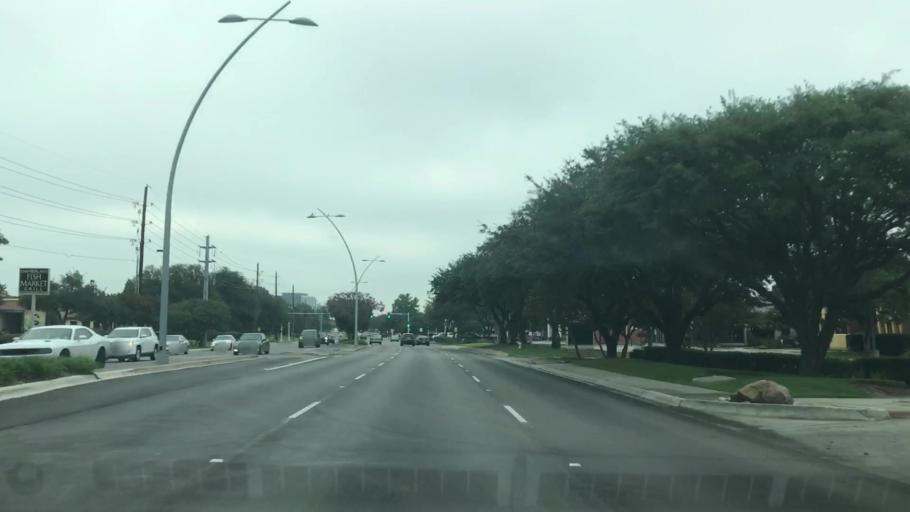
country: US
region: Texas
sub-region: Dallas County
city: Addison
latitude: 32.9542
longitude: -96.8362
